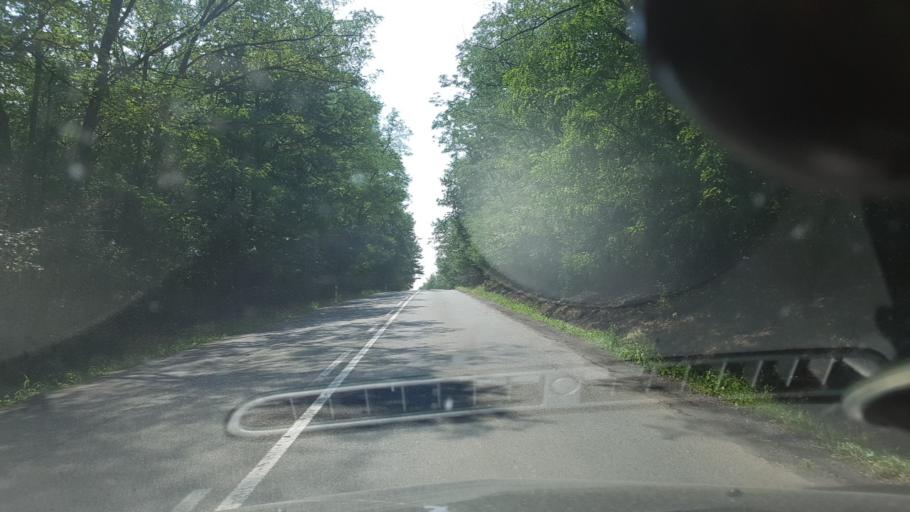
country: SK
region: Banskobystricky
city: Velky Krtis
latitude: 48.2526
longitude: 19.4258
